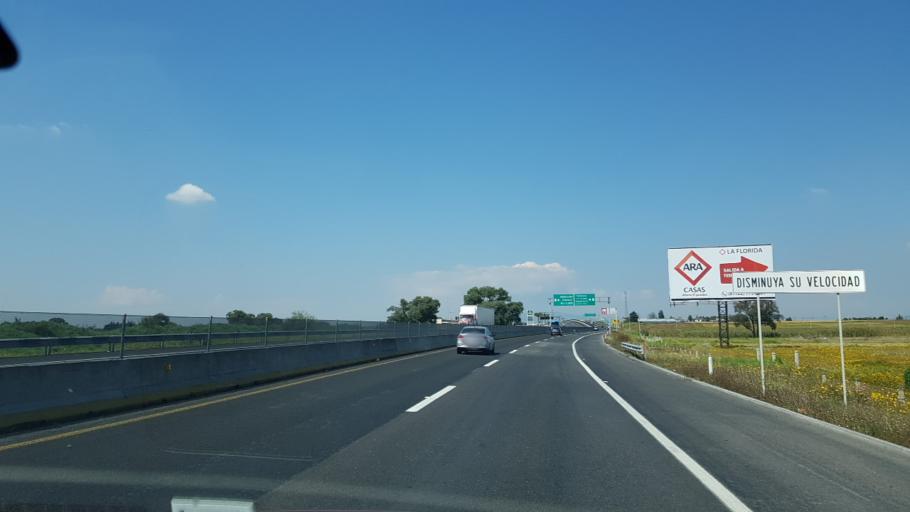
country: MX
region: Mexico
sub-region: Temoaya
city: Llano de la Y
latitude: 19.4085
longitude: -99.6108
